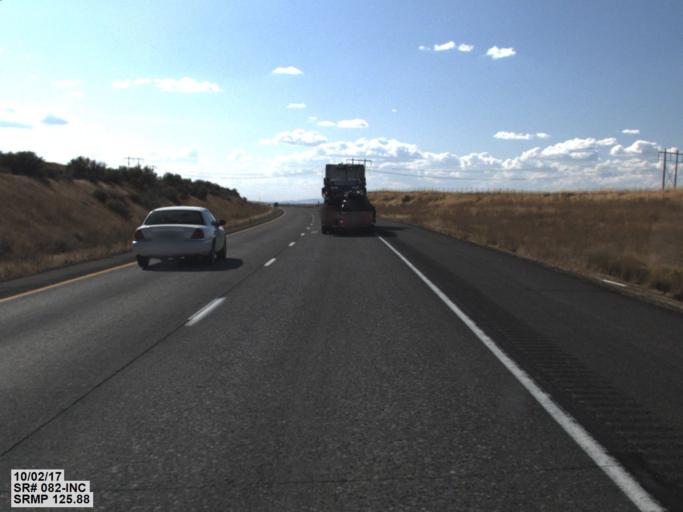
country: US
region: Oregon
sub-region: Umatilla County
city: Umatilla
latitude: 45.9975
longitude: -119.2707
